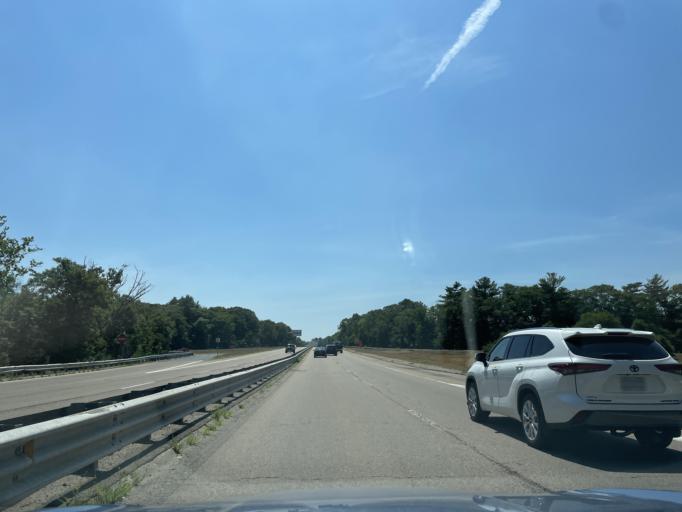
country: US
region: Massachusetts
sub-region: Norfolk County
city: Randolph
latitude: 42.1595
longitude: -71.0656
